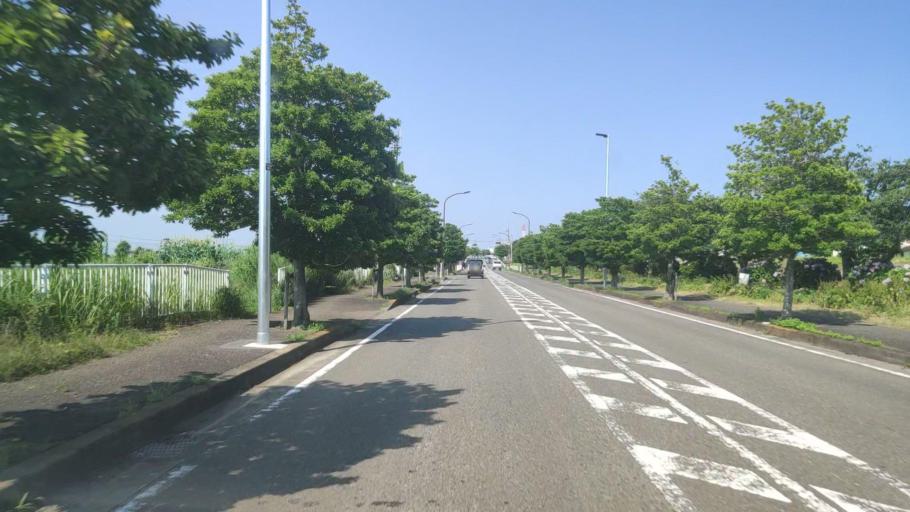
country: JP
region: Kanagawa
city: Hiratsuka
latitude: 35.3539
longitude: 139.3316
